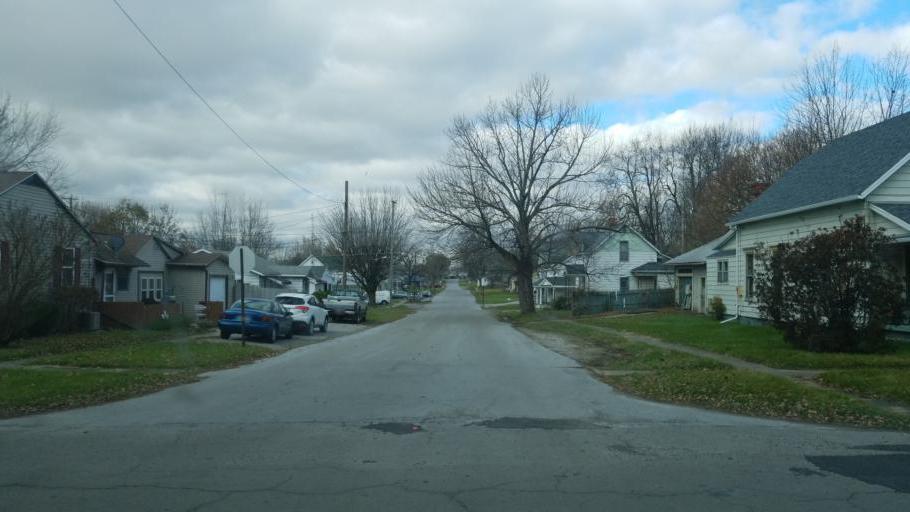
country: US
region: Ohio
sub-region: Hardin County
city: Kenton
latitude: 40.6495
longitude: -83.6133
